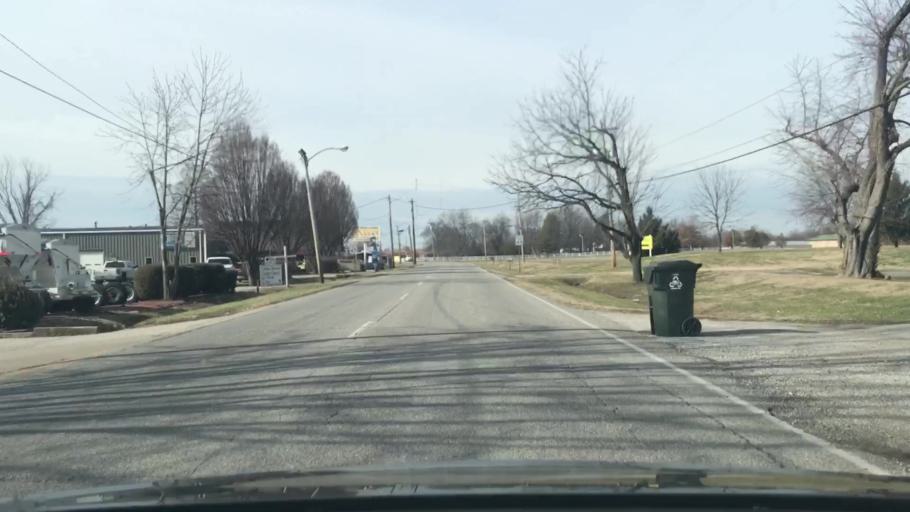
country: US
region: Kentucky
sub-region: Daviess County
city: Owensboro
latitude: 37.7739
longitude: -87.1448
